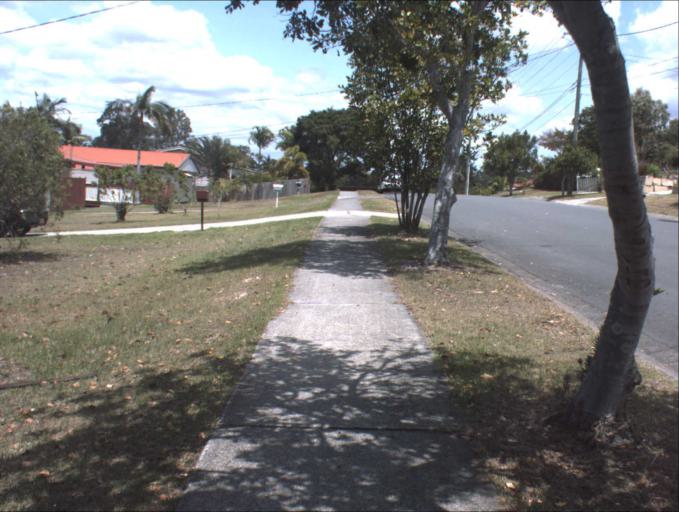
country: AU
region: Queensland
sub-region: Logan
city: Woodridge
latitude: -27.6244
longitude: 153.1030
